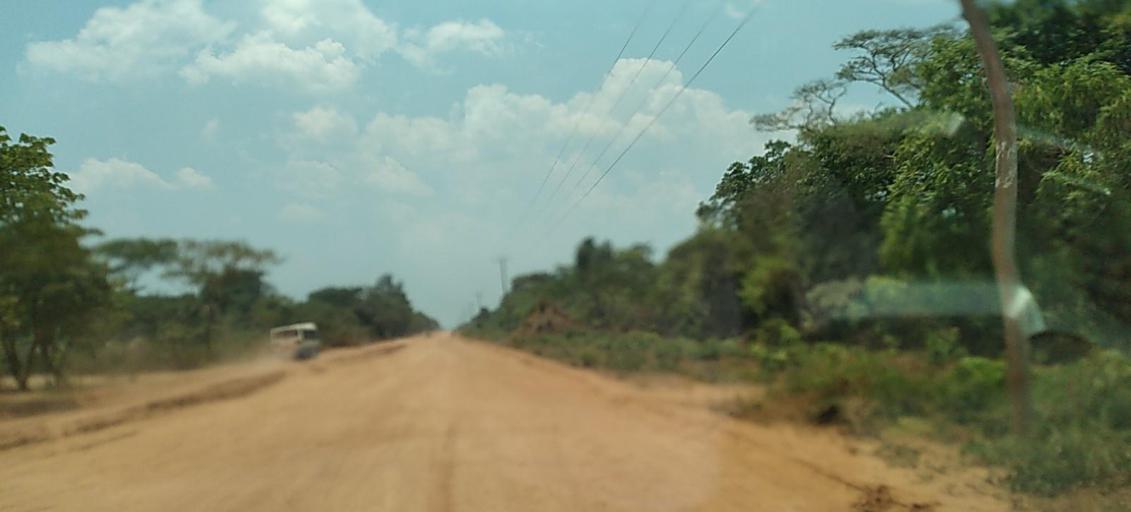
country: ZM
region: Copperbelt
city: Chingola
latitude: -12.9018
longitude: 27.5717
